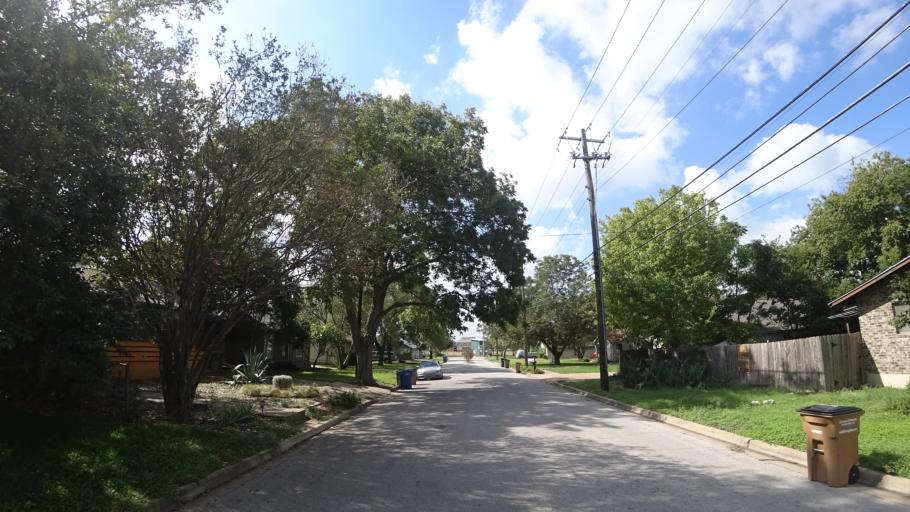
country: US
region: Texas
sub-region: Travis County
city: Austin
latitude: 30.3465
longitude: -97.7180
